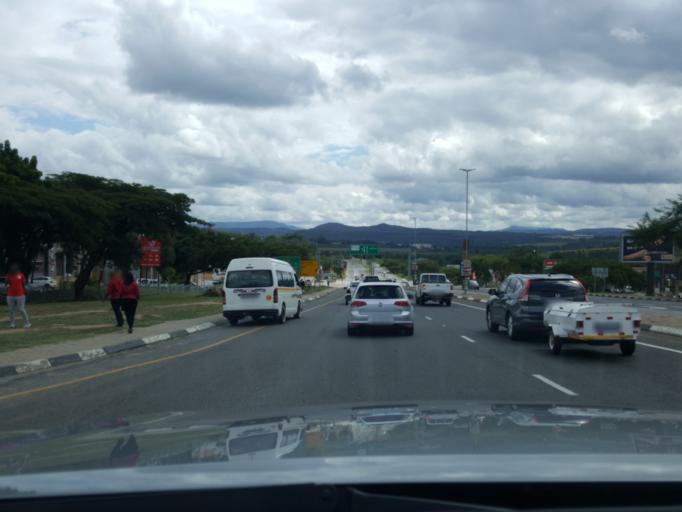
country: ZA
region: Mpumalanga
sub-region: Ehlanzeni District
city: Nelspruit
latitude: -25.4706
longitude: 30.9604
